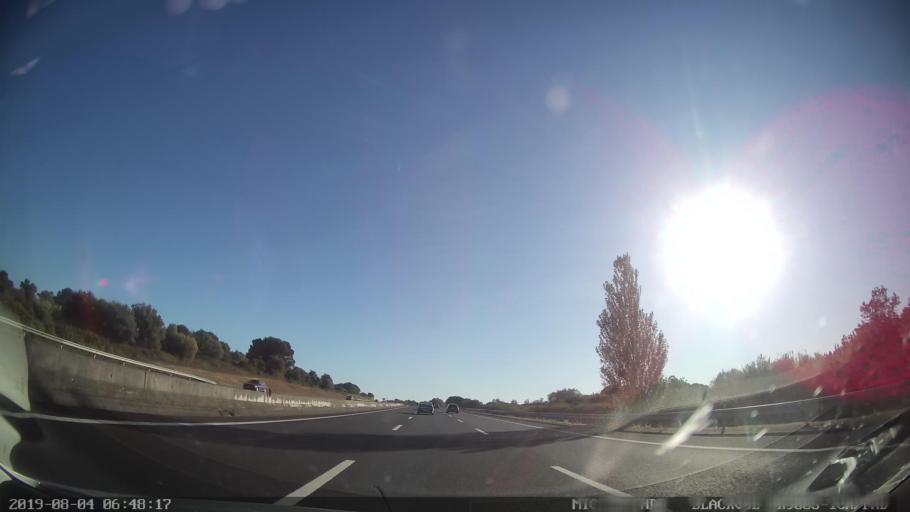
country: PT
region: Santarem
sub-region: Cartaxo
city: Cartaxo
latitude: 39.1947
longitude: -8.8161
